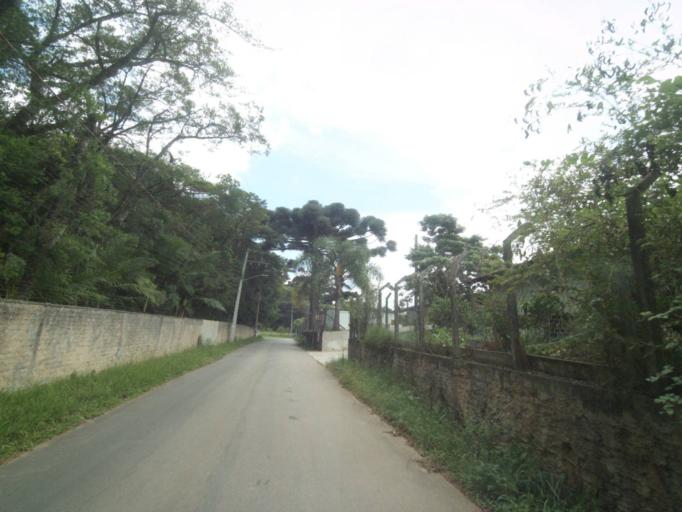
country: BR
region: Parana
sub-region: Curitiba
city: Curitiba
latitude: -25.4677
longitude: -49.3432
